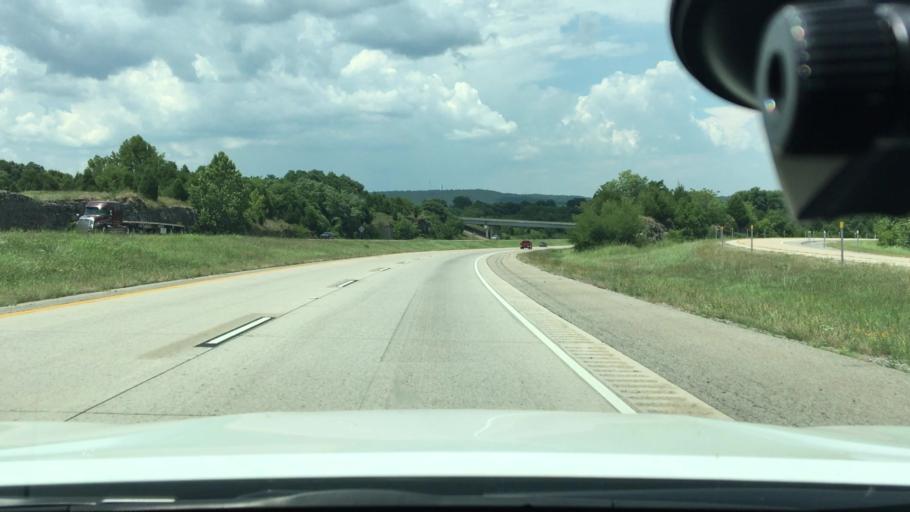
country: US
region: Arkansas
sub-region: Washington County
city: West Fork
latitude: 35.9209
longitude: -94.1991
